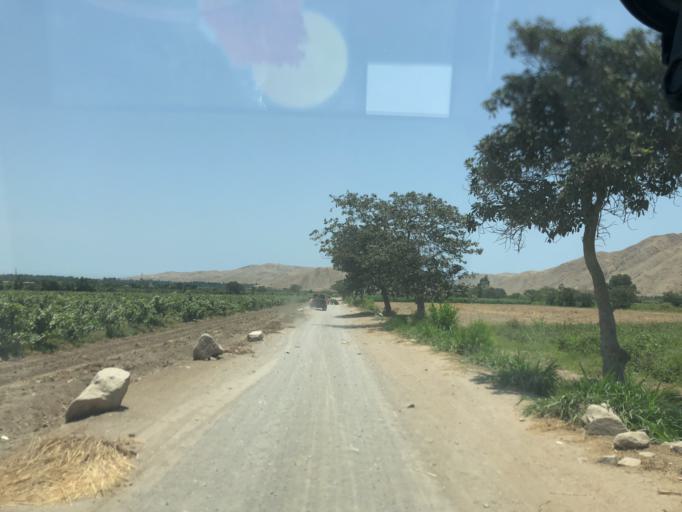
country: PE
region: Lima
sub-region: Provincia de Canete
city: Quilmana
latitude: -12.9681
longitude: -76.4157
